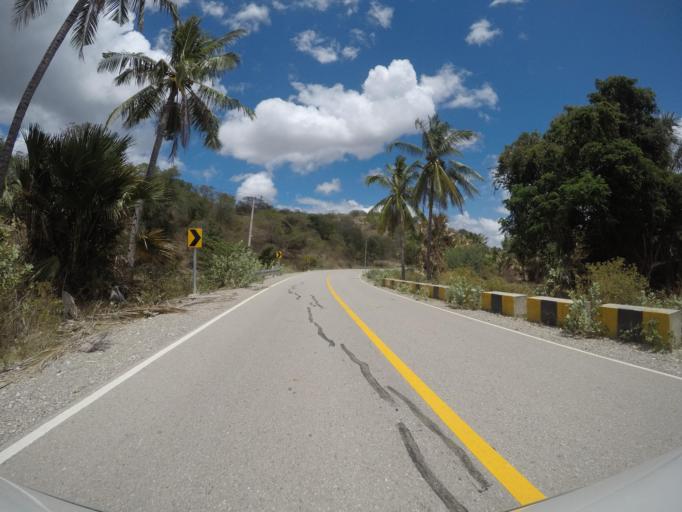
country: TL
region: Lautem
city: Lospalos
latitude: -8.4146
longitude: 126.8042
